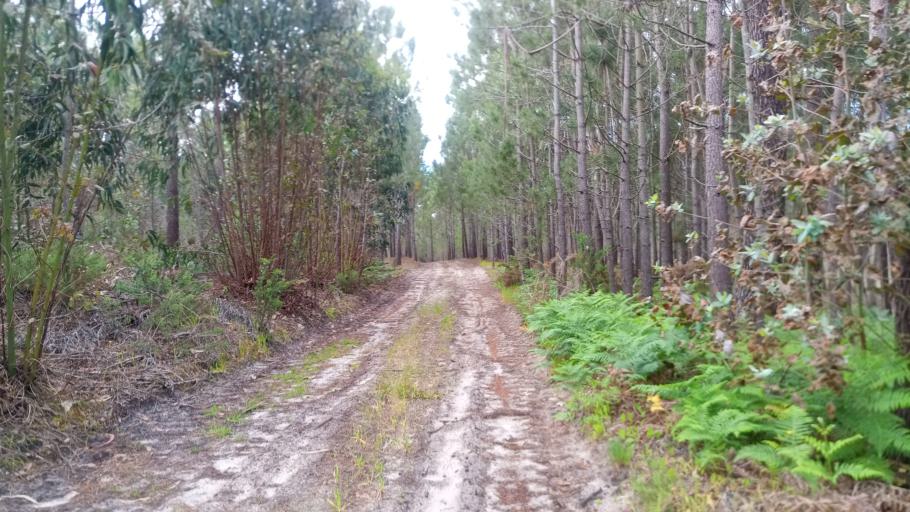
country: PT
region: Leiria
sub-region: Caldas da Rainha
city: Caldas da Rainha
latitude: 39.4471
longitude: -9.1663
